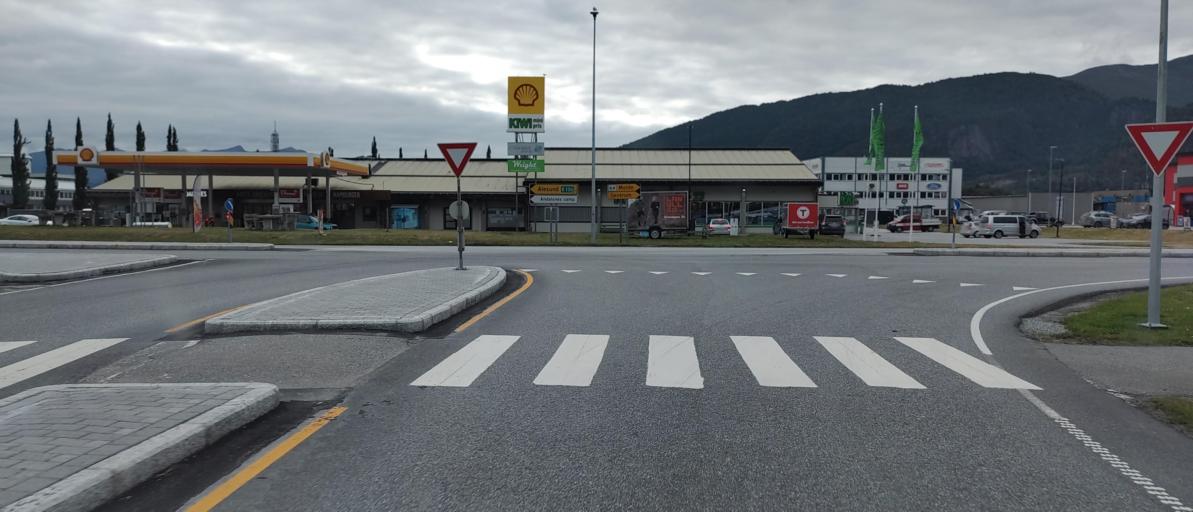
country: NO
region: More og Romsdal
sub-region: Rauma
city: Andalsnes
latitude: 62.5585
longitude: 7.6835
